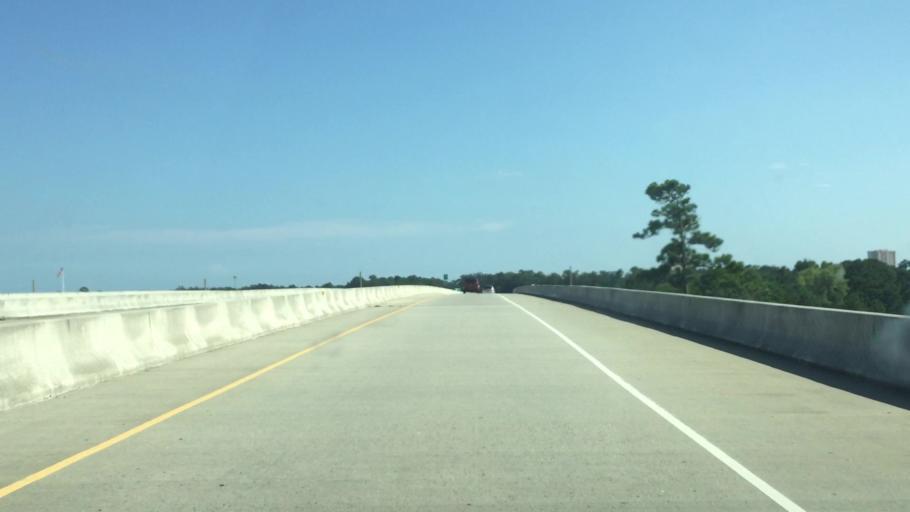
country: US
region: South Carolina
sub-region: Horry County
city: North Myrtle Beach
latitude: 33.7905
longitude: -78.7775
